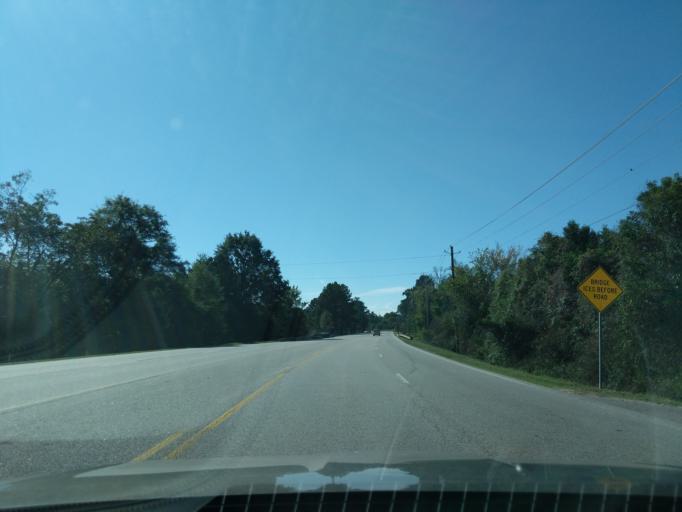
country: US
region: Georgia
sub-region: Richmond County
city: Augusta
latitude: 33.4240
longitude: -82.0063
